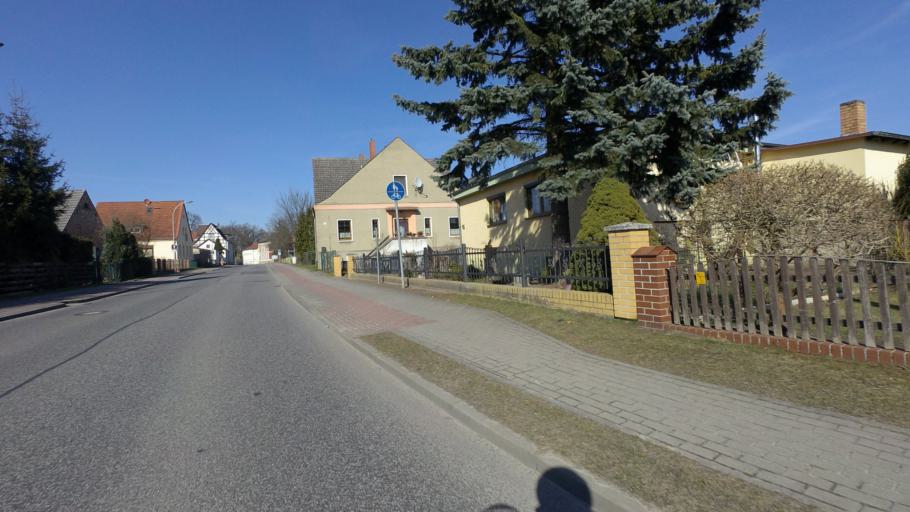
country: DE
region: Brandenburg
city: Angermunde
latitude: 53.0123
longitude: 14.0005
